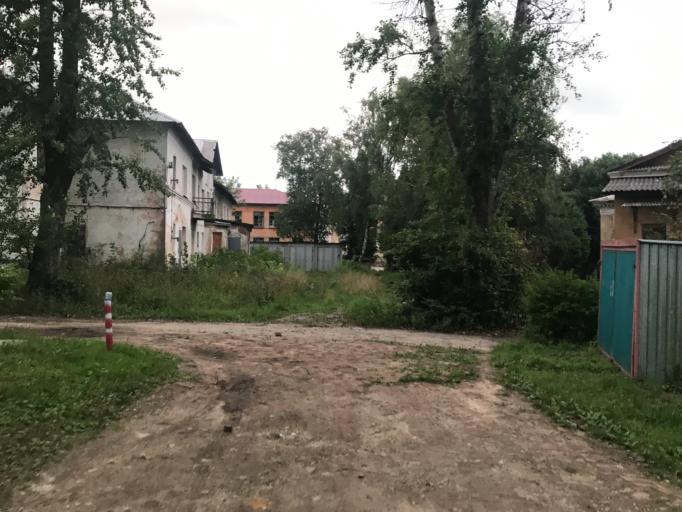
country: RU
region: Tula
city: Priupskiy
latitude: 53.9406
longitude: 37.7021
